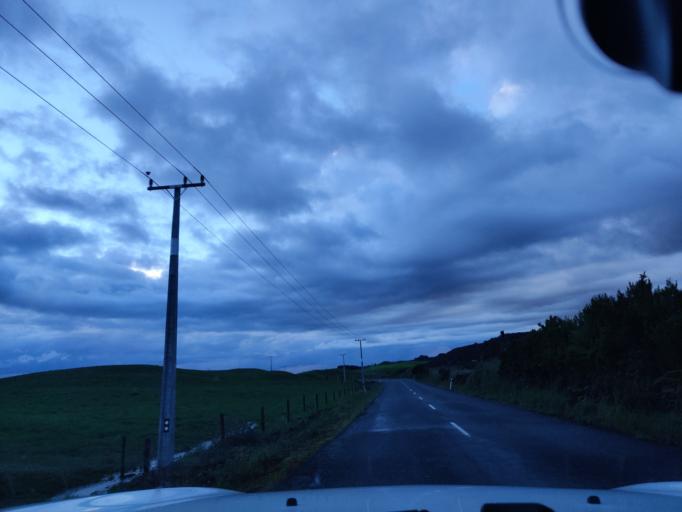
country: NZ
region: Waikato
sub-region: South Waikato District
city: Tokoroa
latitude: -38.1691
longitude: 175.7690
